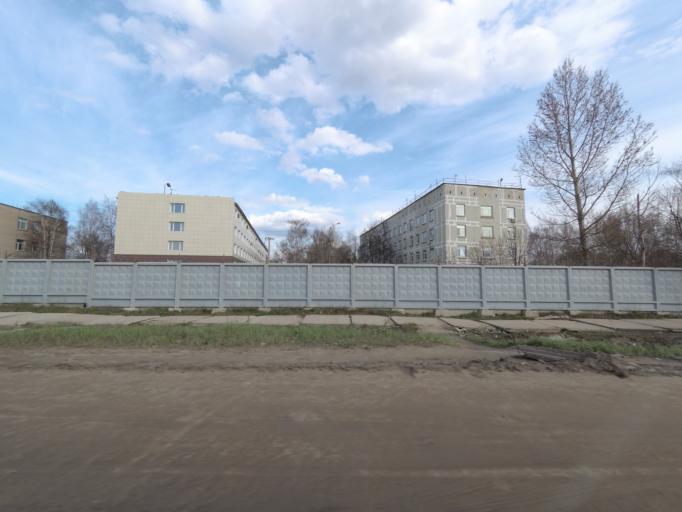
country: RU
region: Moskovskaya
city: Lobnya
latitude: 55.9885
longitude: 37.4162
